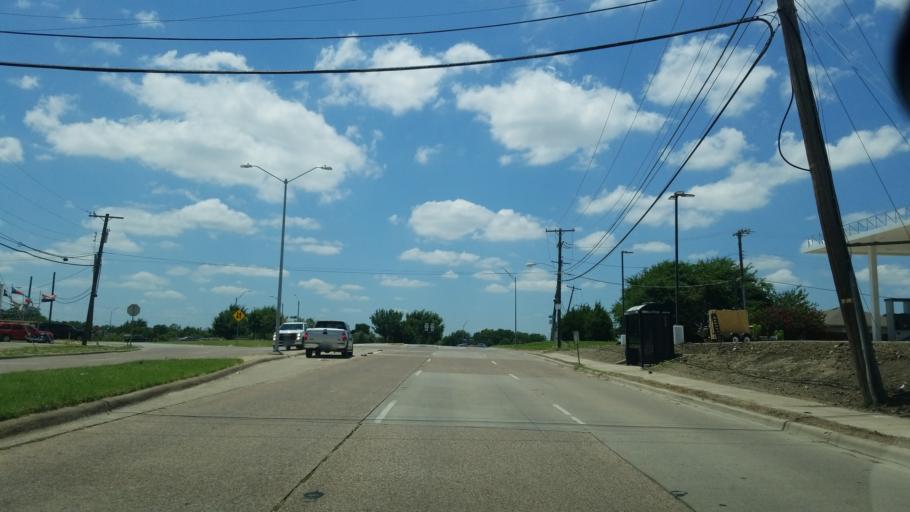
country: US
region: Texas
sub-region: Dallas County
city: Hutchins
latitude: 32.7344
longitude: -96.7110
